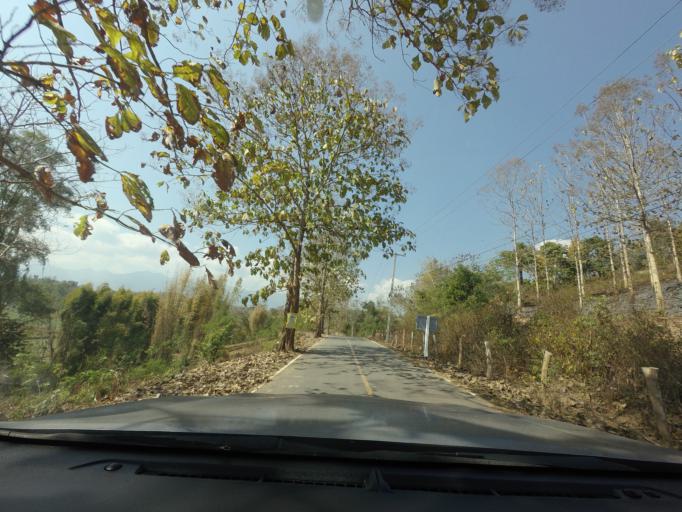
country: TH
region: Mae Hong Son
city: Wiang Nuea
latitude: 19.4024
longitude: 98.4476
